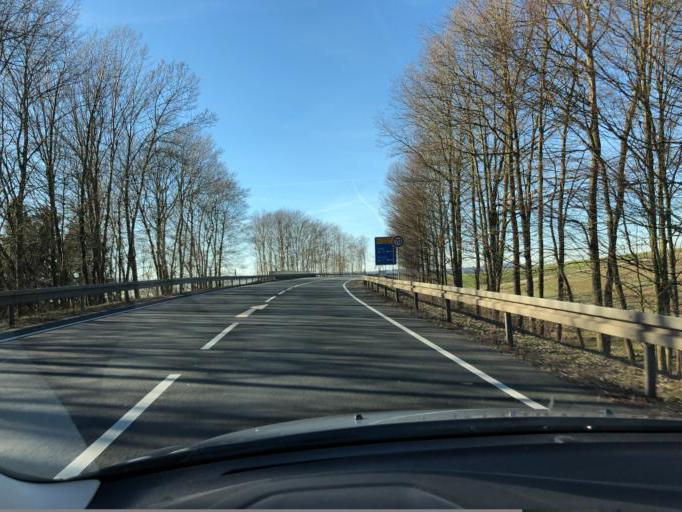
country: DE
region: Lower Saxony
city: Seesen
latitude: 51.9466
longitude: 10.1504
